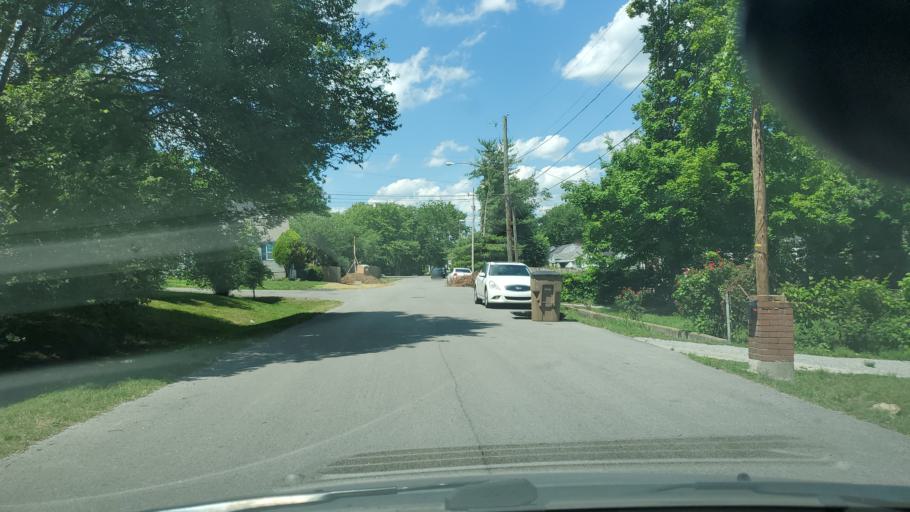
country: US
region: Tennessee
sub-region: Davidson County
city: Nashville
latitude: 36.1982
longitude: -86.7510
